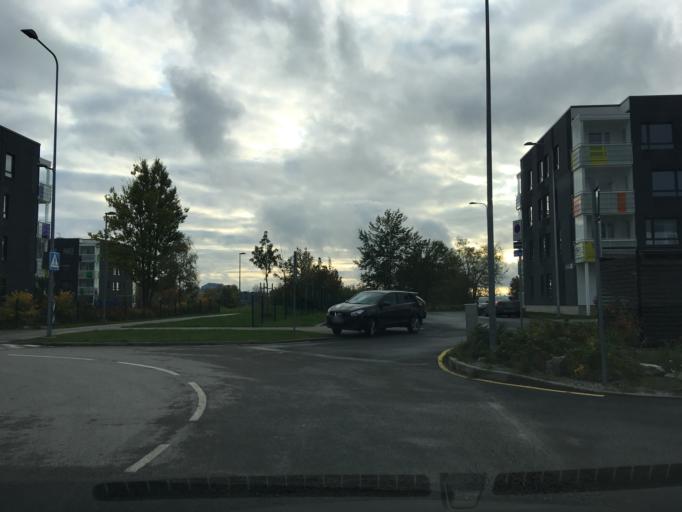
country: EE
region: Harju
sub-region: Tallinna linn
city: Tallinn
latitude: 59.4333
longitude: 24.8079
